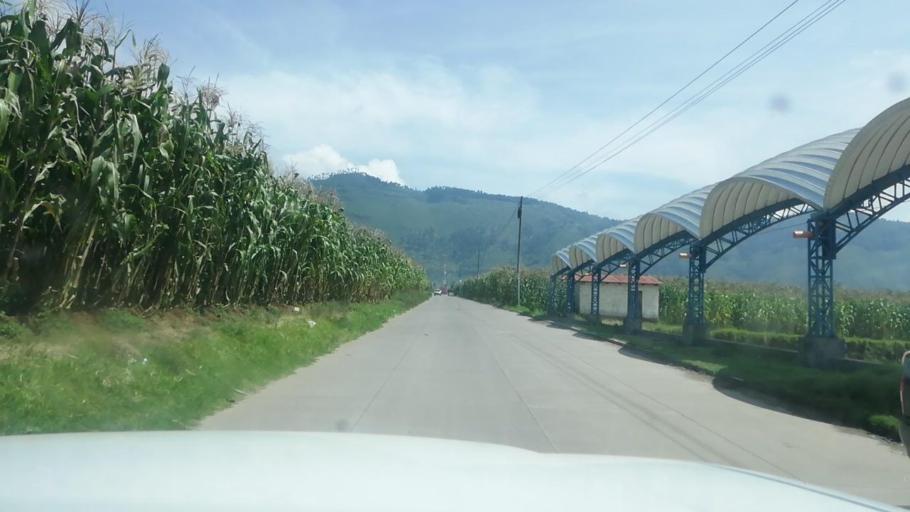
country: GT
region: Totonicapan
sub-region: Municipio de San Andres Xecul
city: San Andres Xecul
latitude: 14.8938
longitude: -91.4776
